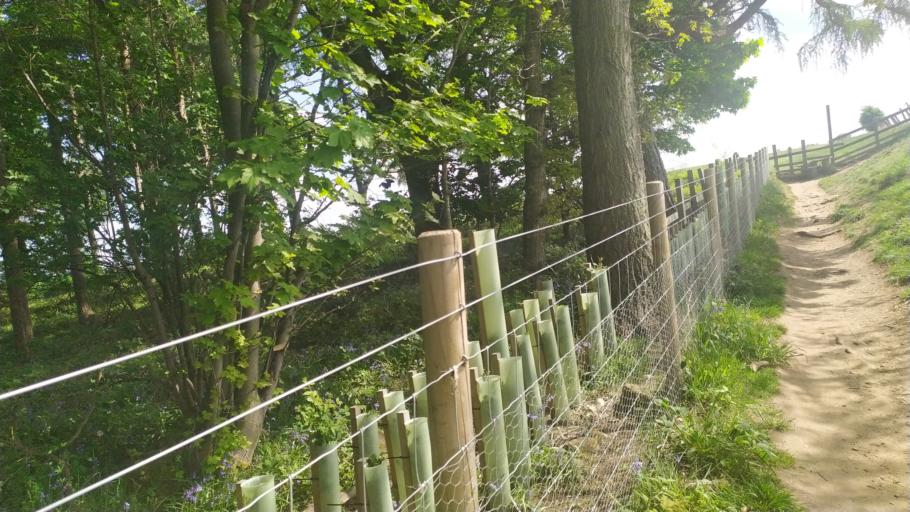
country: GB
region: England
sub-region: City and Borough of Leeds
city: Chapel Allerton
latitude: 53.8693
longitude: -1.5612
